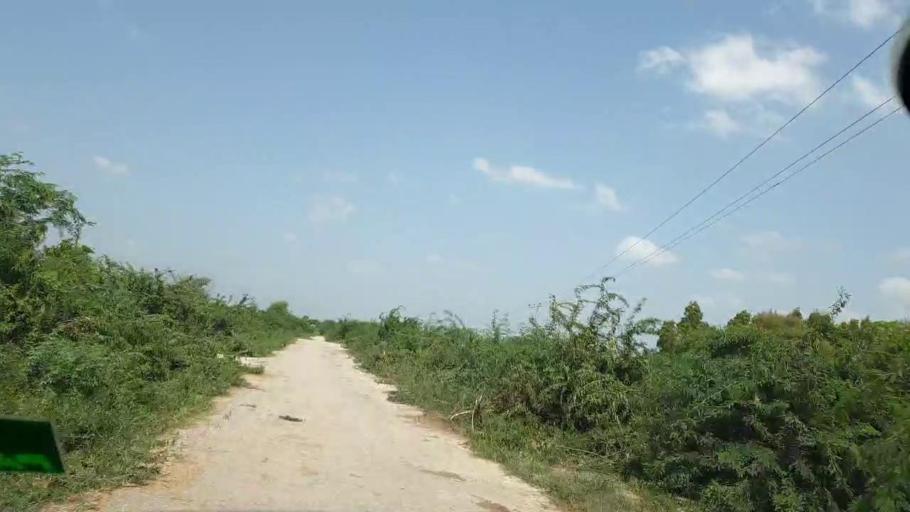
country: PK
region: Sindh
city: Kadhan
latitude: 24.5507
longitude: 69.2110
